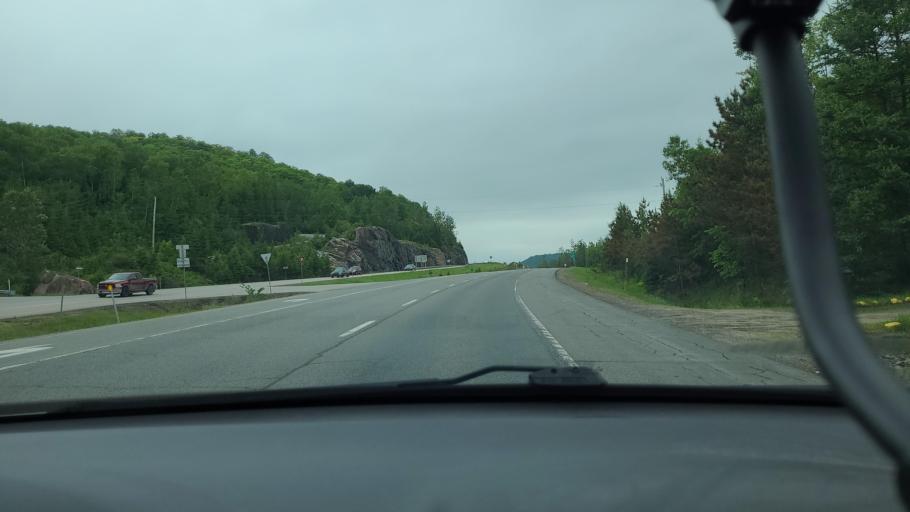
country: CA
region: Quebec
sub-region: Laurentides
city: Mont-Tremblant
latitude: 46.1361
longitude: -74.6291
